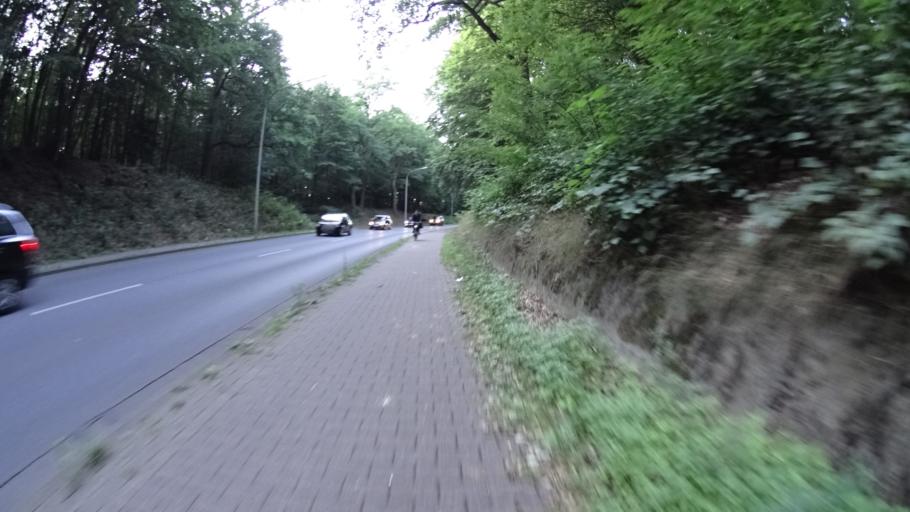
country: DE
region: Lower Saxony
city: Lueneburg
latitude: 53.2268
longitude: 10.3941
